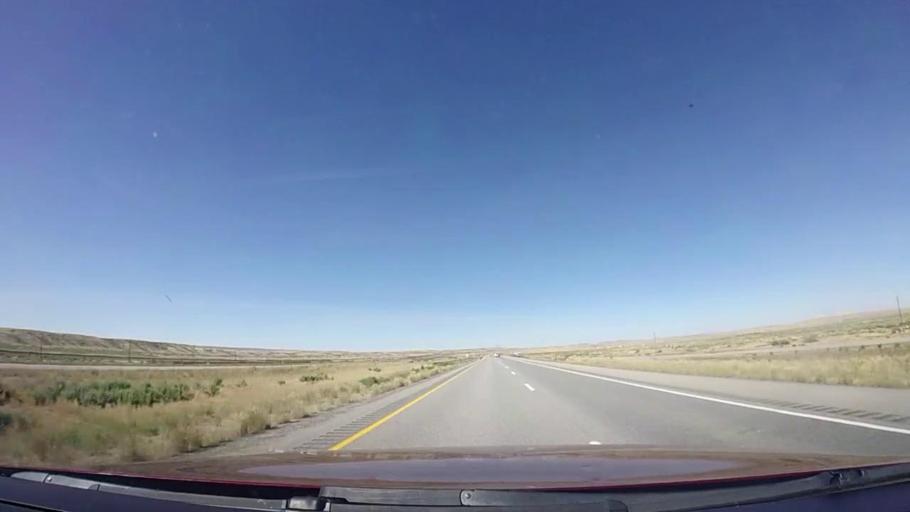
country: US
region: Wyoming
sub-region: Carbon County
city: Rawlins
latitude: 41.6521
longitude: -108.1271
